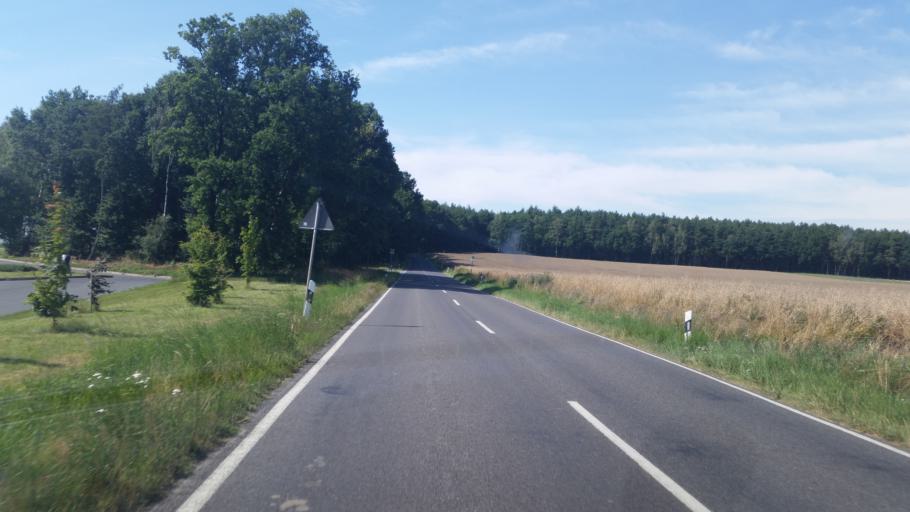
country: DE
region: Saxony
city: Kamenz
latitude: 51.2969
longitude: 14.0520
